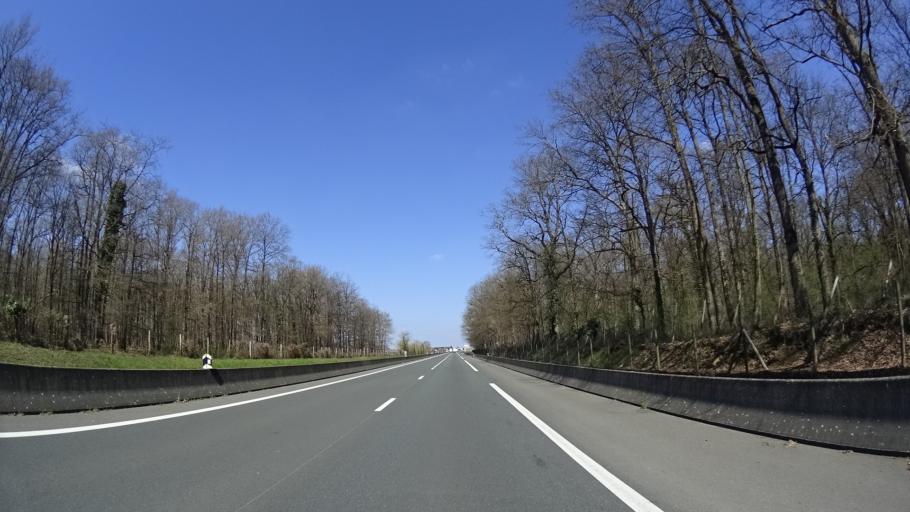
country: FR
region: Pays de la Loire
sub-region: Departement de Maine-et-Loire
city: Doue-la-Fontaine
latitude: 47.2181
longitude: -0.3058
